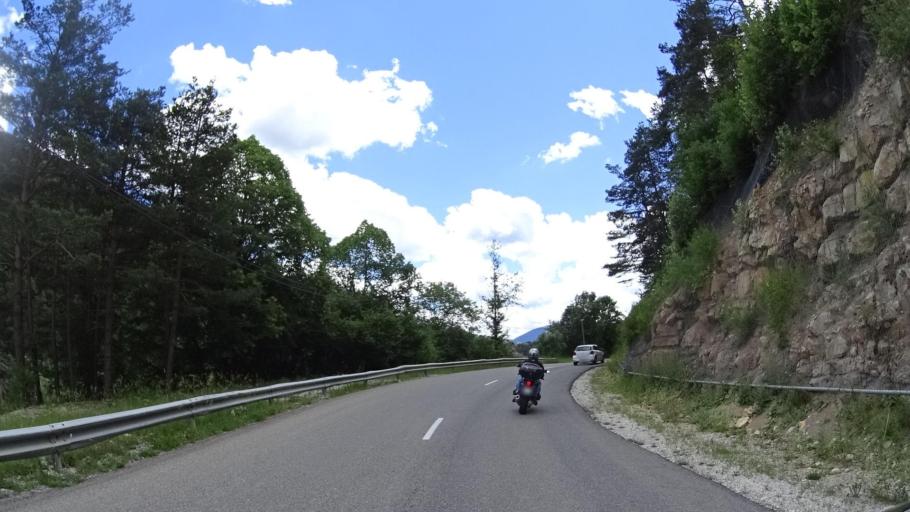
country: FR
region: Provence-Alpes-Cote d'Azur
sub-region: Departement des Alpes-de-Haute-Provence
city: Annot
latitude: 44.0206
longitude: 6.5555
